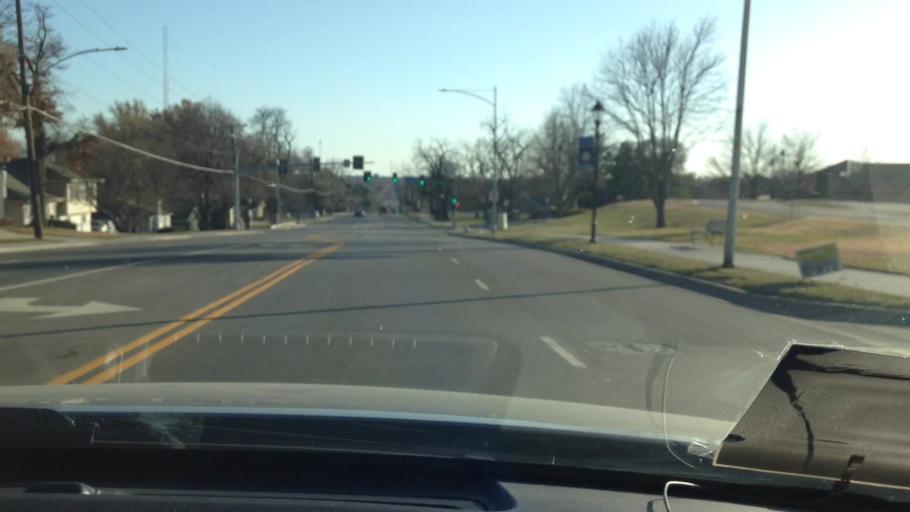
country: US
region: Kansas
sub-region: Johnson County
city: Prairie Village
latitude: 38.9905
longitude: -94.6305
